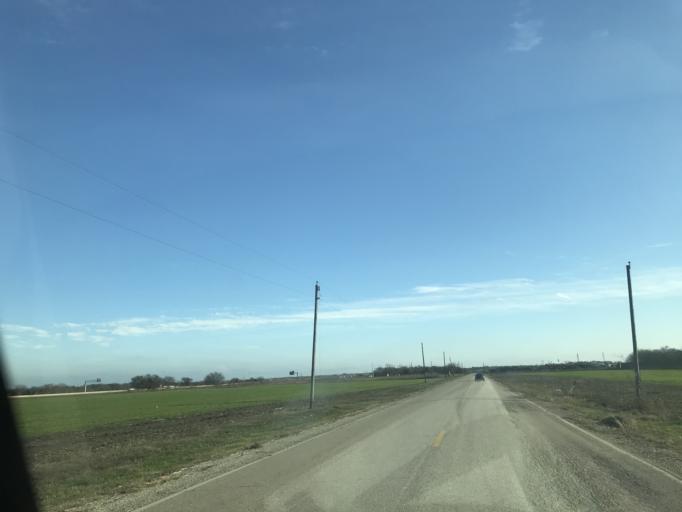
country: US
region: Texas
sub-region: Dallas County
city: Wilmer
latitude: 32.5714
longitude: -96.6727
